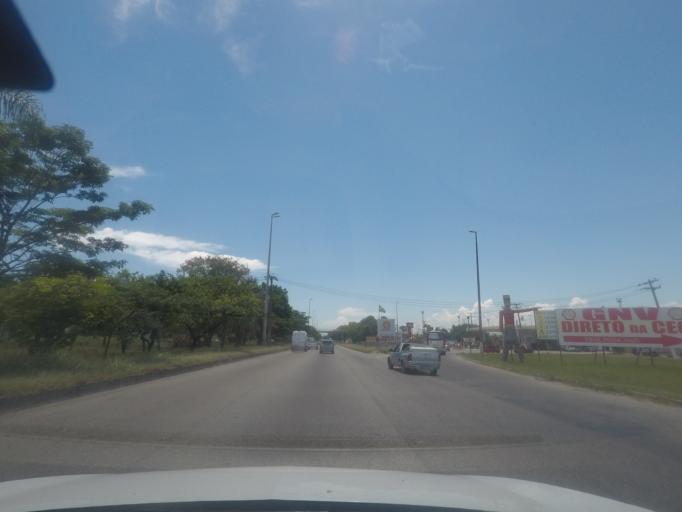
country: BR
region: Rio de Janeiro
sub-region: Itaguai
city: Itaguai
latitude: -22.8926
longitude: -43.6725
